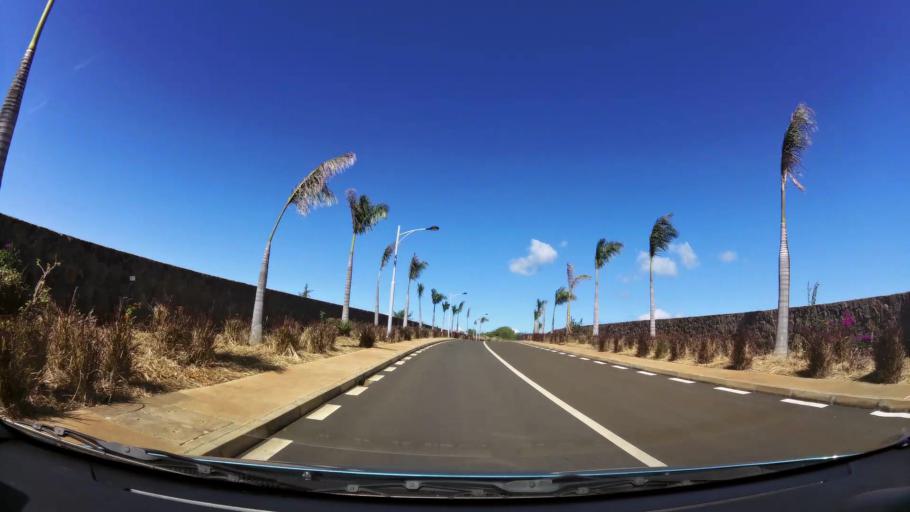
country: MU
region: Black River
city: Flic en Flac
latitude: -20.2697
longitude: 57.3820
